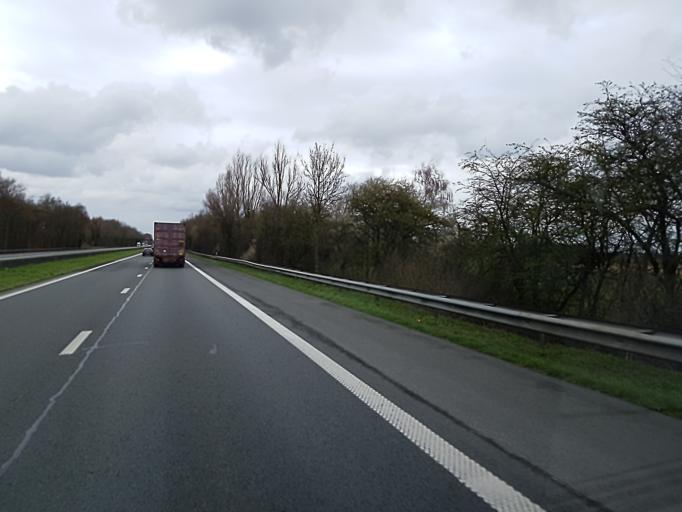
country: BE
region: Wallonia
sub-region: Province du Hainaut
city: Pecq
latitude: 50.6380
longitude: 3.3051
